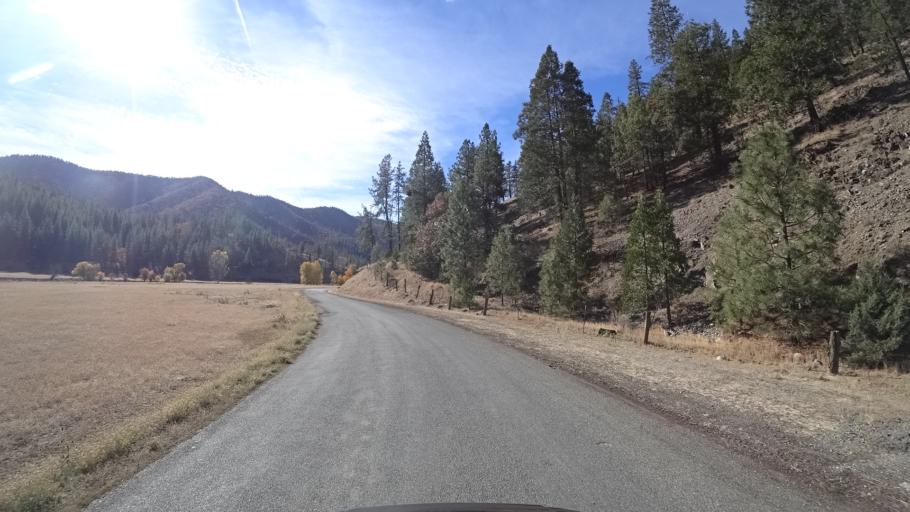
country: US
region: California
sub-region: Siskiyou County
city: Yreka
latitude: 41.6242
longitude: -122.7153
